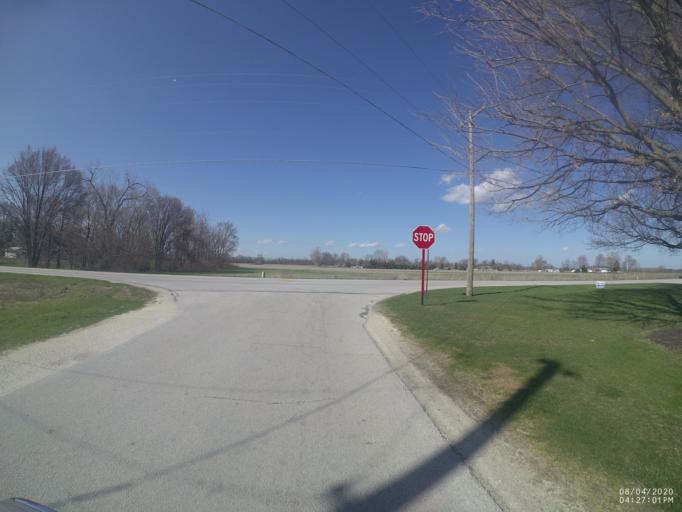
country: US
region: Ohio
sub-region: Sandusky County
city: Stony Prairie
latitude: 41.3257
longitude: -83.2057
